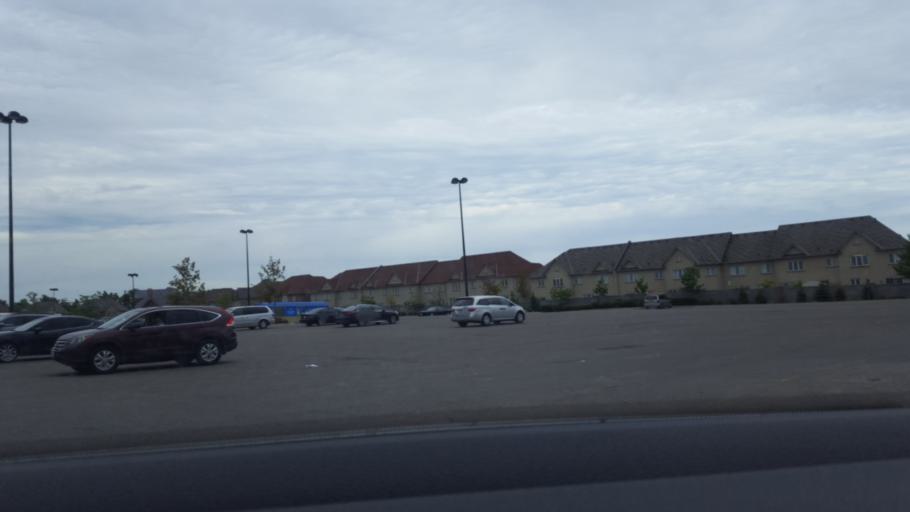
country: CA
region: Ontario
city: Brampton
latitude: 43.6564
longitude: -79.8135
